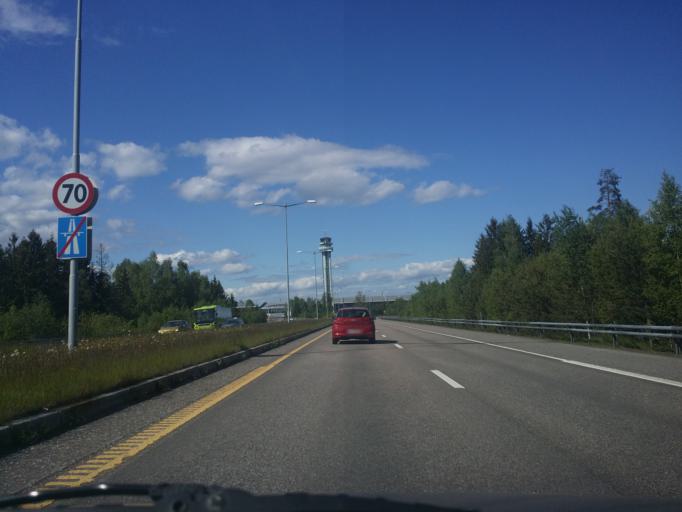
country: NO
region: Akershus
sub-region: Nannestad
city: Teigebyen
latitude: 60.1871
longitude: 11.0951
